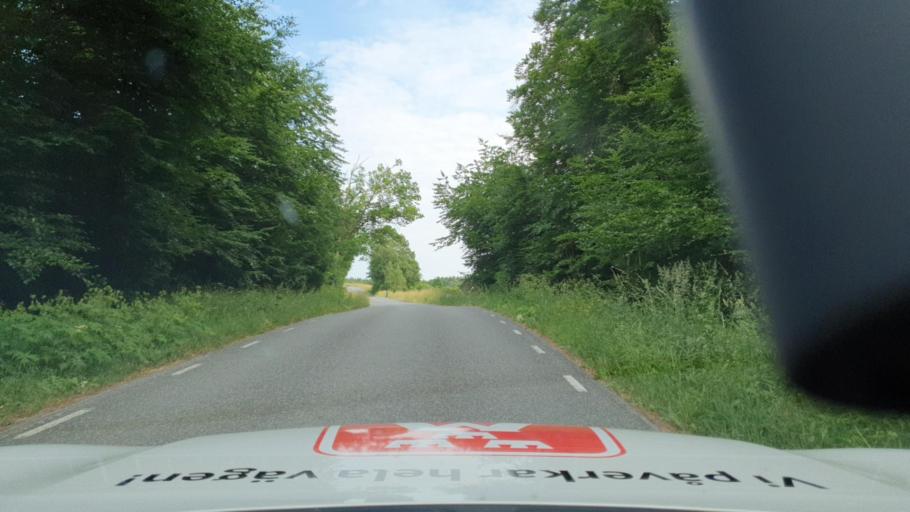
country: SE
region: Skane
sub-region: Kristianstads Kommun
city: Degeberga
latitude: 55.6989
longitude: 14.0562
